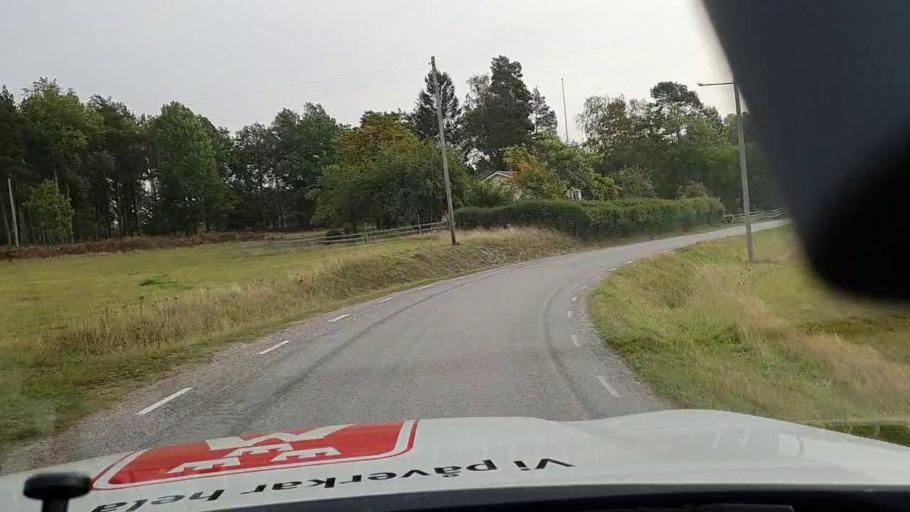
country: SE
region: Soedermanland
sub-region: Nykopings Kommun
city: Stigtomta
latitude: 58.9842
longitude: 16.9273
